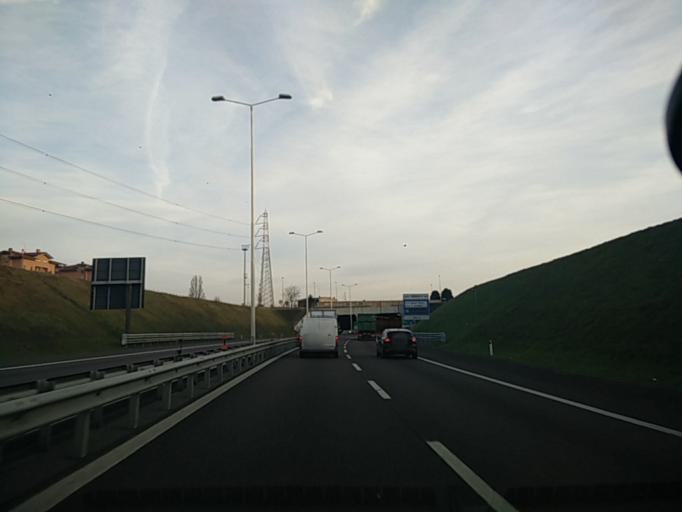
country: IT
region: Lombardy
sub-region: Provincia di Monza e Brianza
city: Muggio
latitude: 45.5752
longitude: 9.2221
